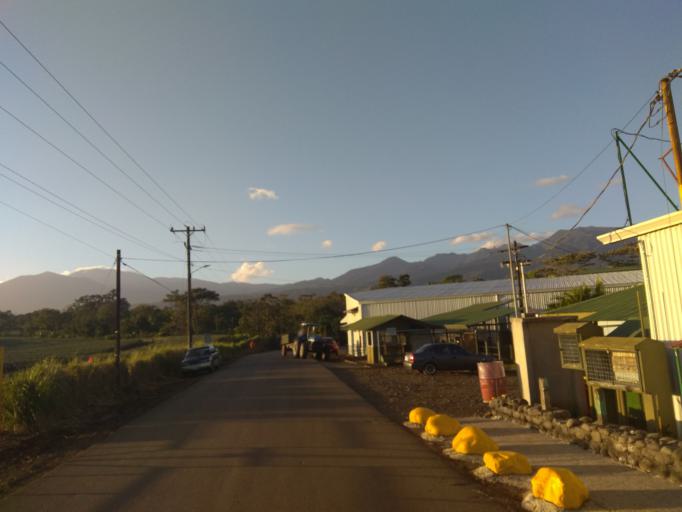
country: CR
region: Alajuela
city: Pital
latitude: 10.3803
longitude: -84.2645
